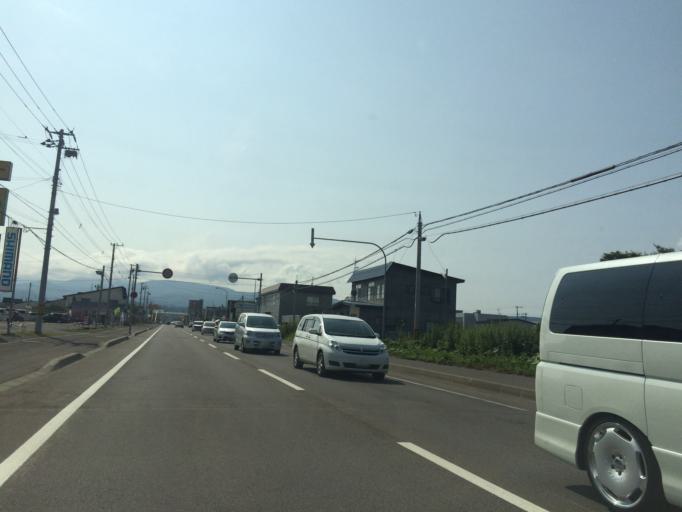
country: JP
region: Hokkaido
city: Yoichi
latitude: 43.1919
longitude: 140.8165
